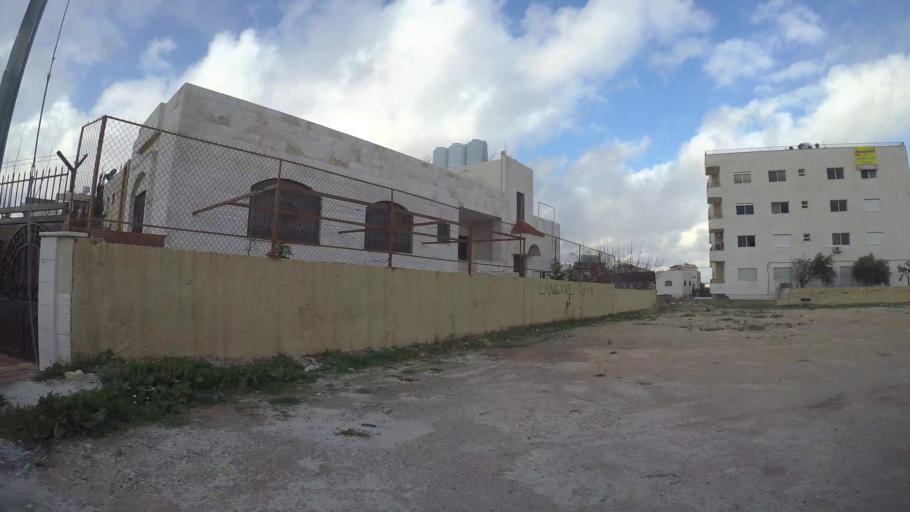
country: JO
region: Amman
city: Al Jubayhah
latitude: 32.0550
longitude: 35.8925
